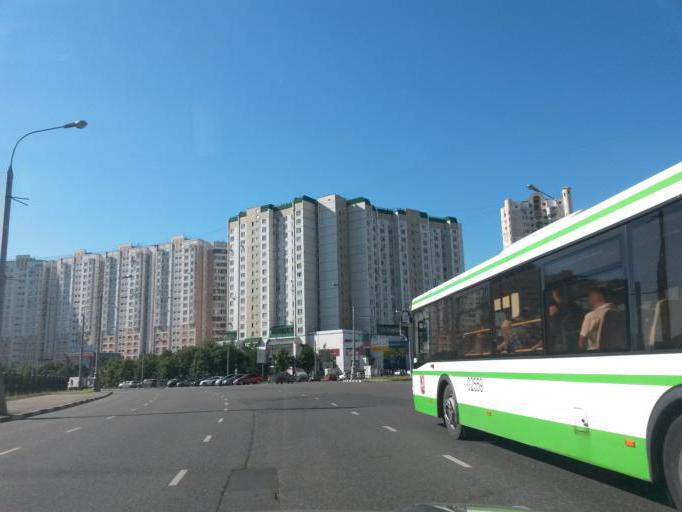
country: RU
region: Moscow
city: Lyublino
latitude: 55.6614
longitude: 37.7530
